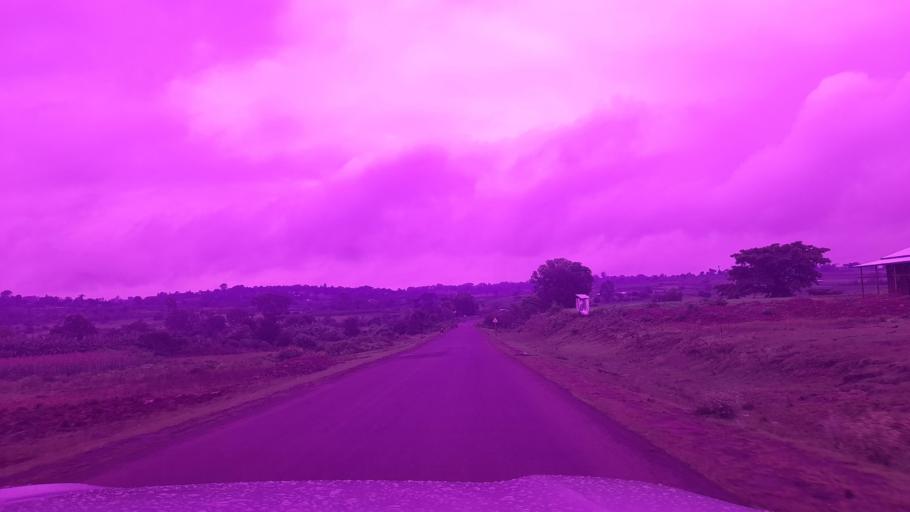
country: ET
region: Oromiya
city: Jima
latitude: 7.6866
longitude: 37.2340
